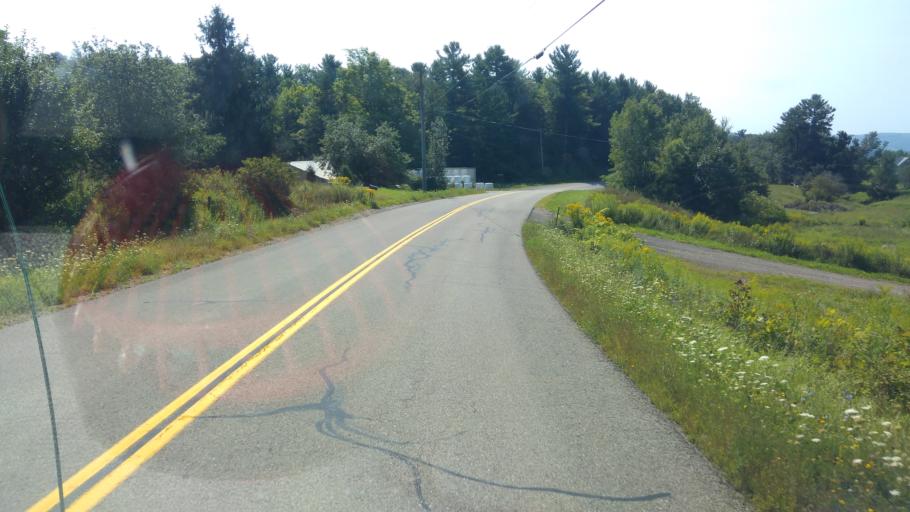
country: US
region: New York
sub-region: Allegany County
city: Belmont
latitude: 42.2746
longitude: -77.9922
